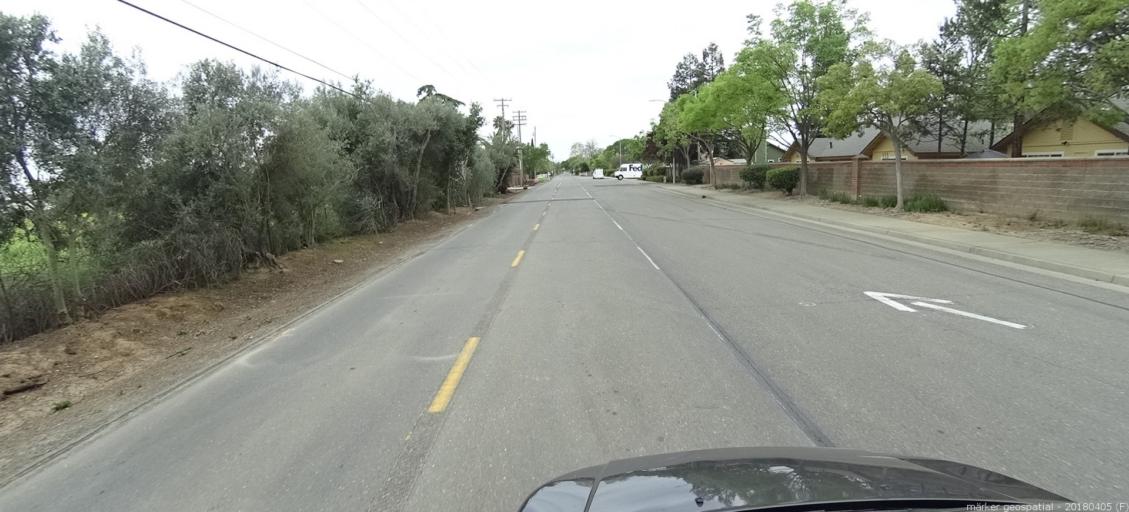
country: US
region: California
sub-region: Sacramento County
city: Galt
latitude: 38.2474
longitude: -121.3166
